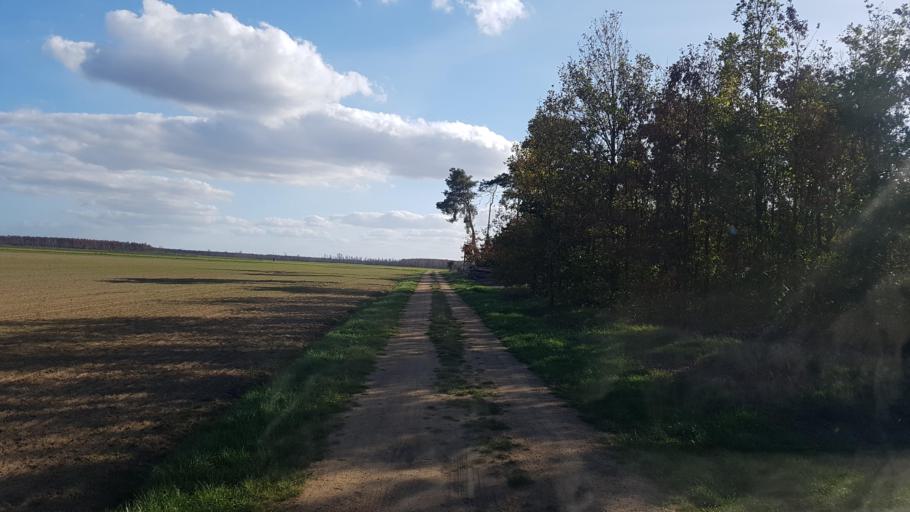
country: DE
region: Brandenburg
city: Muhlberg
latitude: 51.4461
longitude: 13.3109
